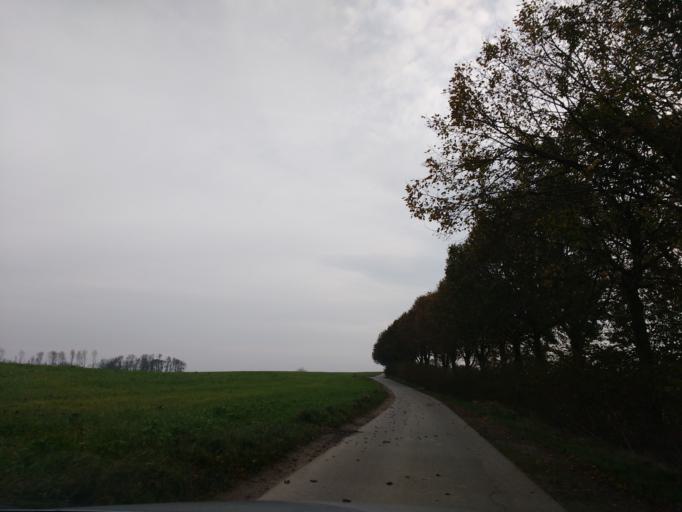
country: DE
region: Mecklenburg-Vorpommern
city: Klutz
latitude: 54.0060
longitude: 11.1553
